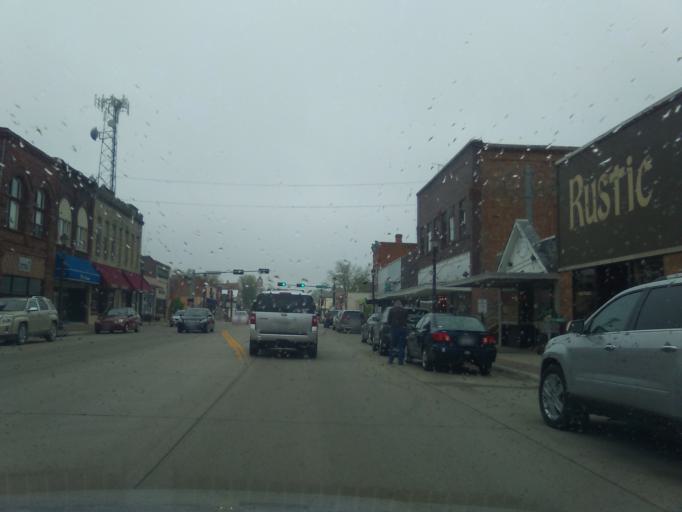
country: US
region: Nebraska
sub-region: Wayne County
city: Wayne
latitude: 42.2306
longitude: -97.0178
